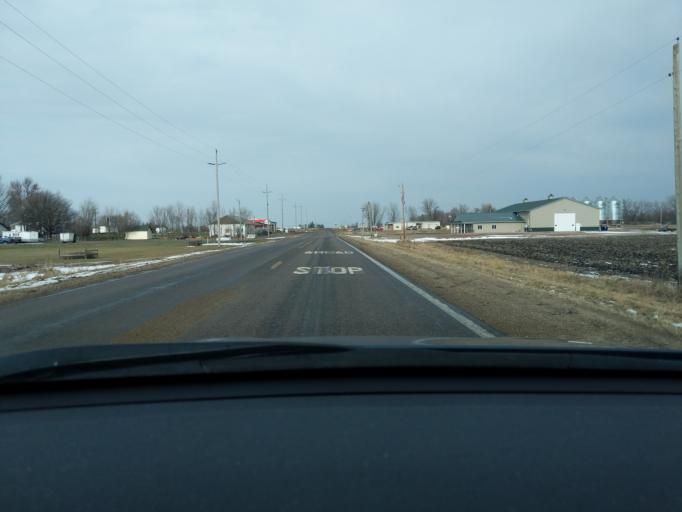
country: US
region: Minnesota
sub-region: Renville County
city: Renville
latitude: 44.7850
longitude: -95.3409
